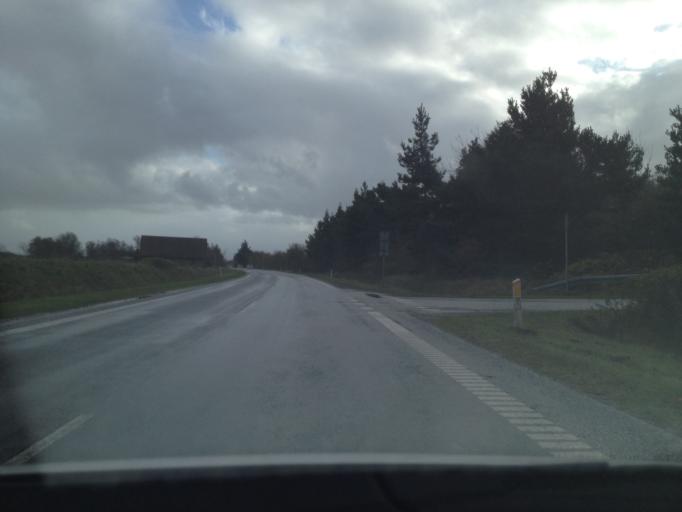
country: DK
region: South Denmark
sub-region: Tonder Kommune
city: Tonder
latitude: 55.0314
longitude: 8.8290
